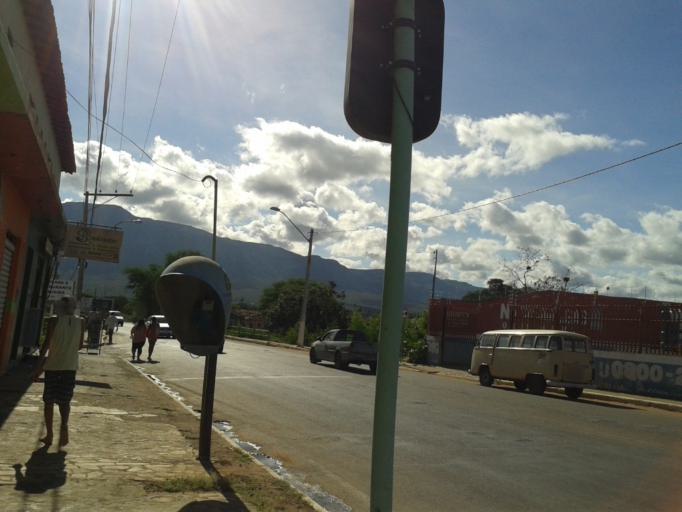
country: BR
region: Bahia
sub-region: Livramento Do Brumado
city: Livramento do Brumado
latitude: -13.6583
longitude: -41.8460
